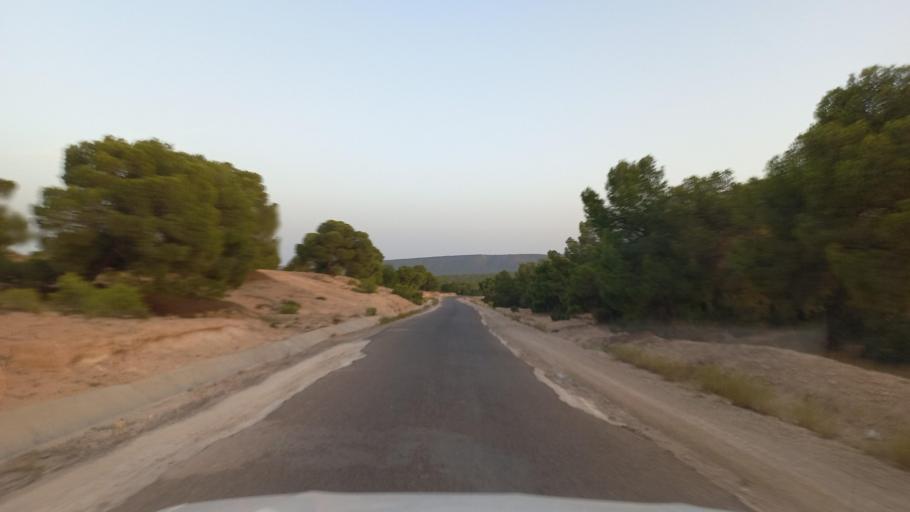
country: TN
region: Al Qasrayn
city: Sbiba
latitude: 35.4194
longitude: 8.9245
